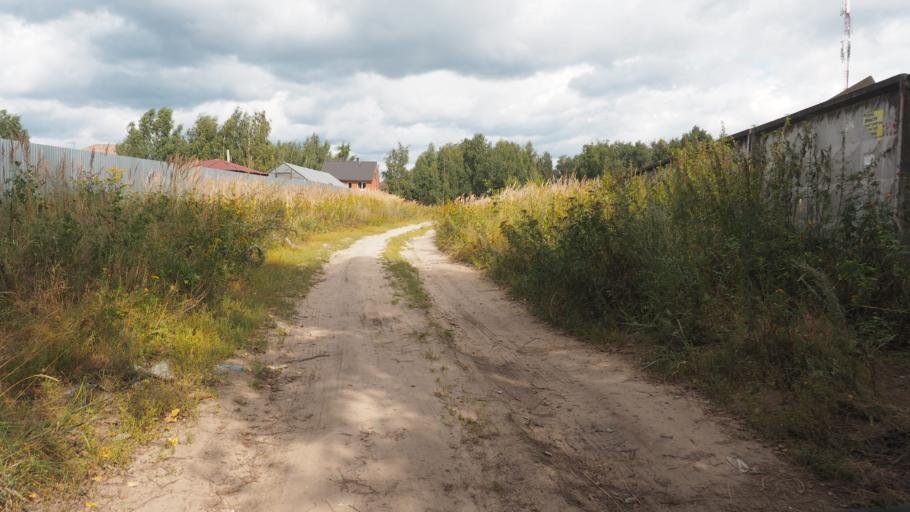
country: RU
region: Moskovskaya
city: Ramenskoye
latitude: 55.5736
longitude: 38.2637
